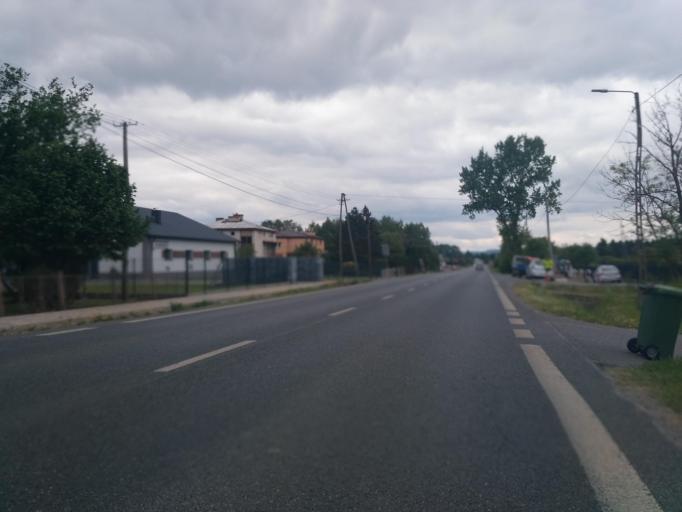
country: PL
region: Subcarpathian Voivodeship
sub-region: Powiat krosnienski
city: Odrzykon
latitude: 49.7262
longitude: 21.7132
